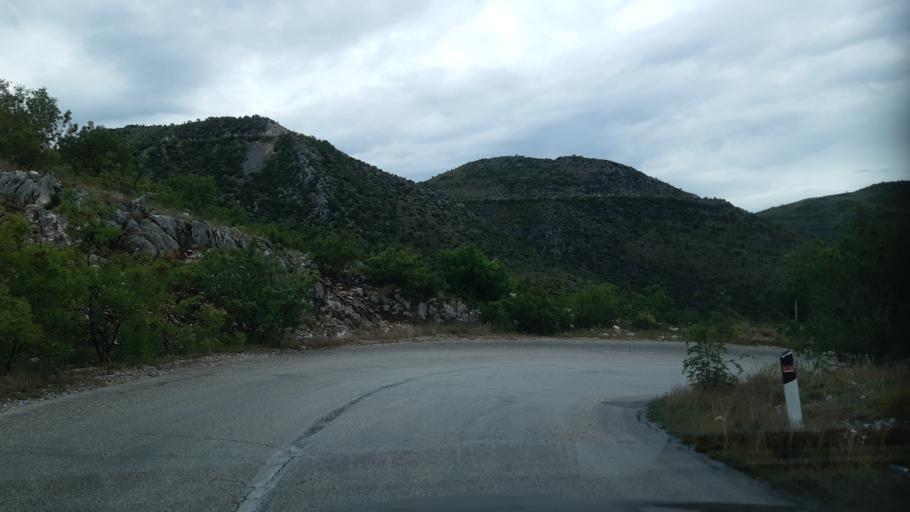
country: BA
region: Federation of Bosnia and Herzegovina
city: Rodoc
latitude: 43.3109
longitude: 17.7876
